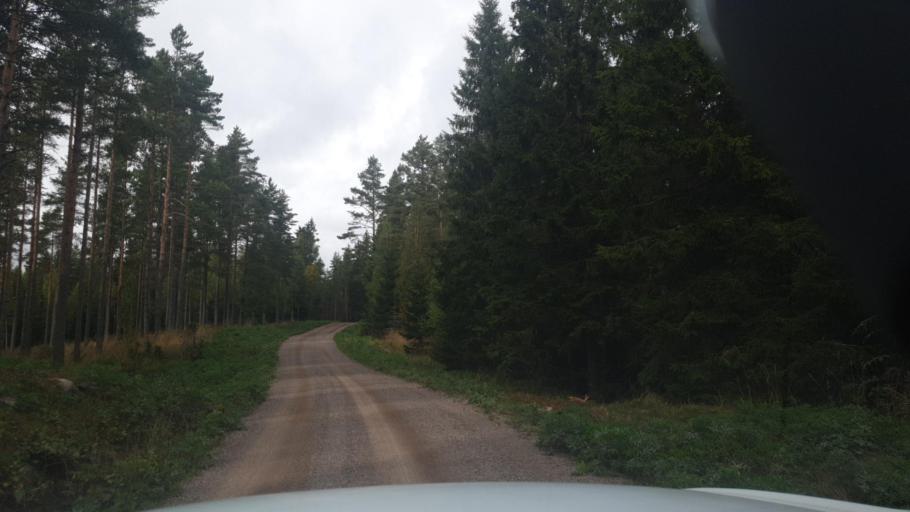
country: SE
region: Vaermland
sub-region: Torsby Kommun
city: Torsby
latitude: 59.9480
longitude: 12.7901
